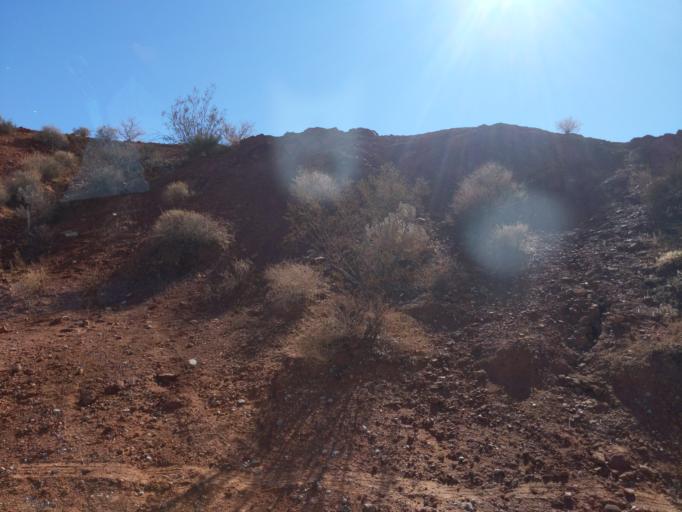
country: US
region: Nevada
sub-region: Clark County
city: Moapa Valley
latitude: 36.4303
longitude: -114.4813
